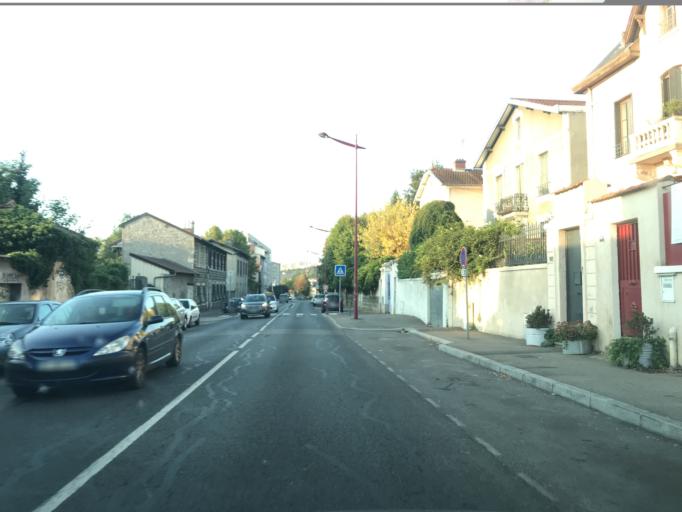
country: FR
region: Rhone-Alpes
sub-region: Departement du Rhone
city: La Mulatiere
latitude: 45.7227
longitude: 4.8117
